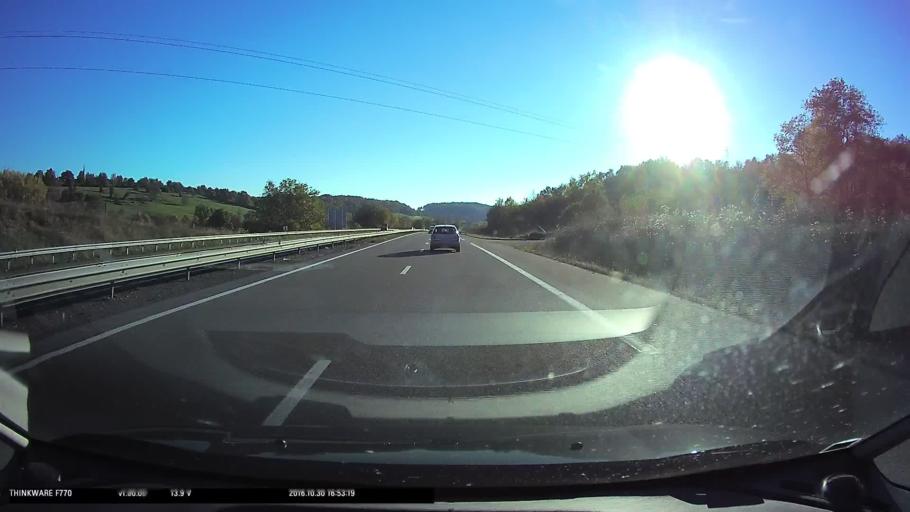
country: FR
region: Franche-Comte
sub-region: Departement du Doubs
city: Chemaudin
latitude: 47.2274
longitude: 5.8844
